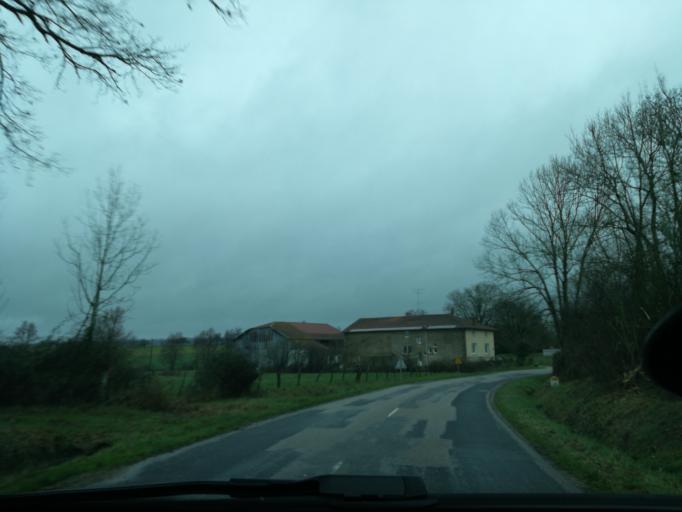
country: FR
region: Lorraine
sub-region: Departement de la Meuse
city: Clermont-en-Argonne
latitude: 48.9972
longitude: 5.0967
